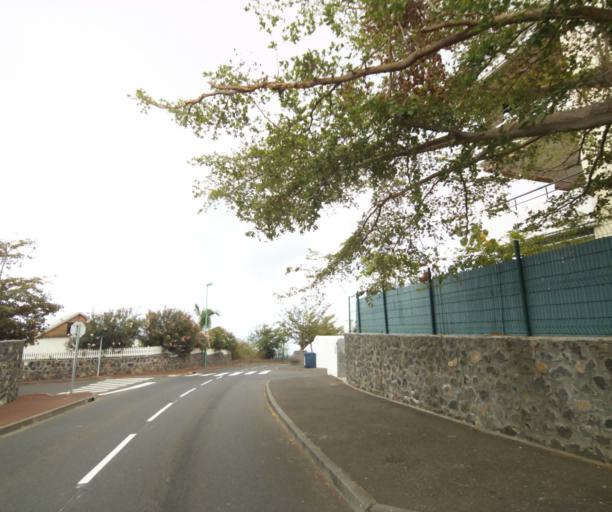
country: RE
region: Reunion
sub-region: Reunion
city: Saint-Paul
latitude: -21.0655
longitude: 55.2283
